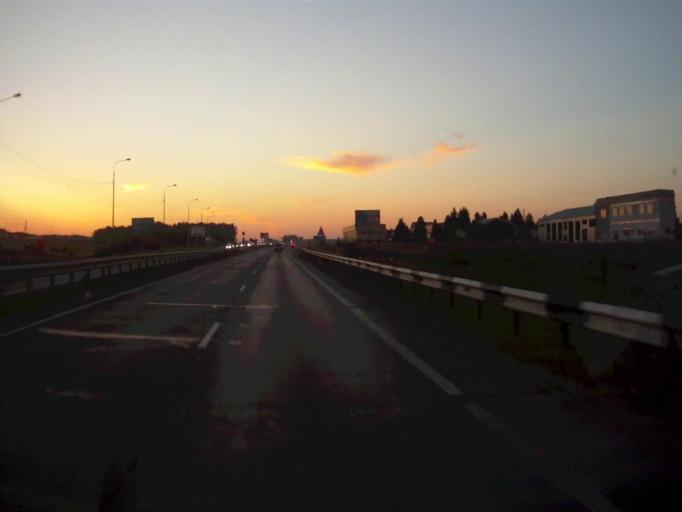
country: RU
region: Chelyabinsk
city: Roshchino
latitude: 55.1811
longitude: 61.2508
